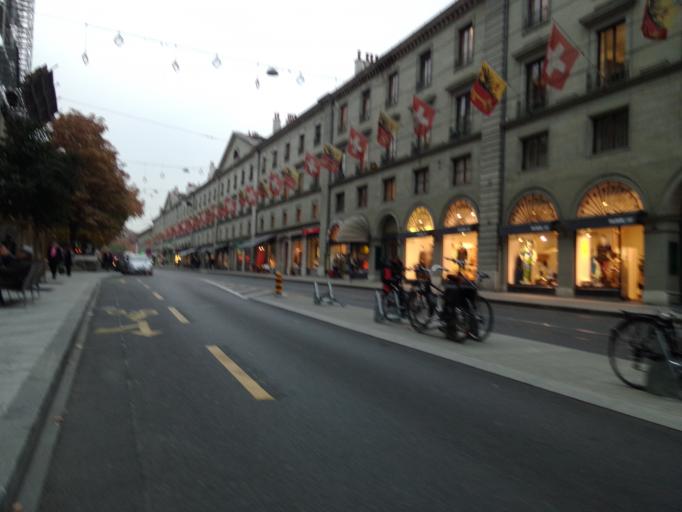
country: CH
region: Geneva
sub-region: Geneva
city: Geneve
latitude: 46.2034
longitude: 6.1431
